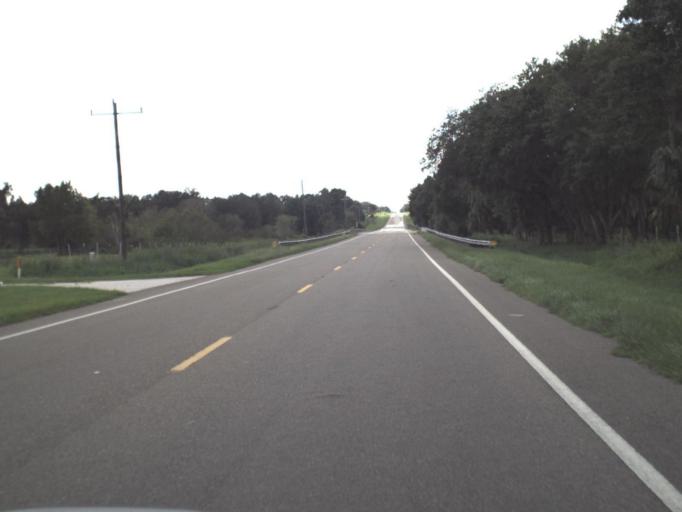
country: US
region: Florida
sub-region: Hardee County
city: Zolfo Springs
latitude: 27.4822
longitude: -81.8598
